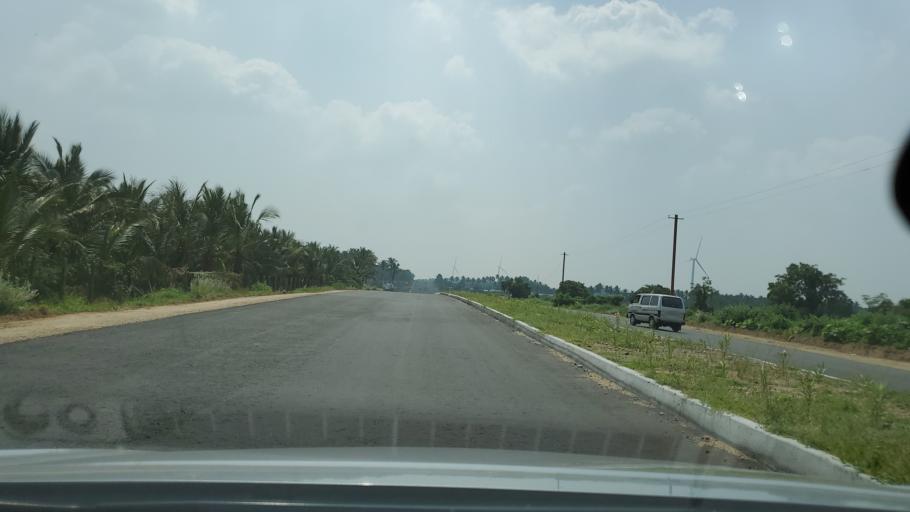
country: IN
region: Tamil Nadu
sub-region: Tiruppur
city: Kangayam
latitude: 10.8873
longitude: 77.4630
